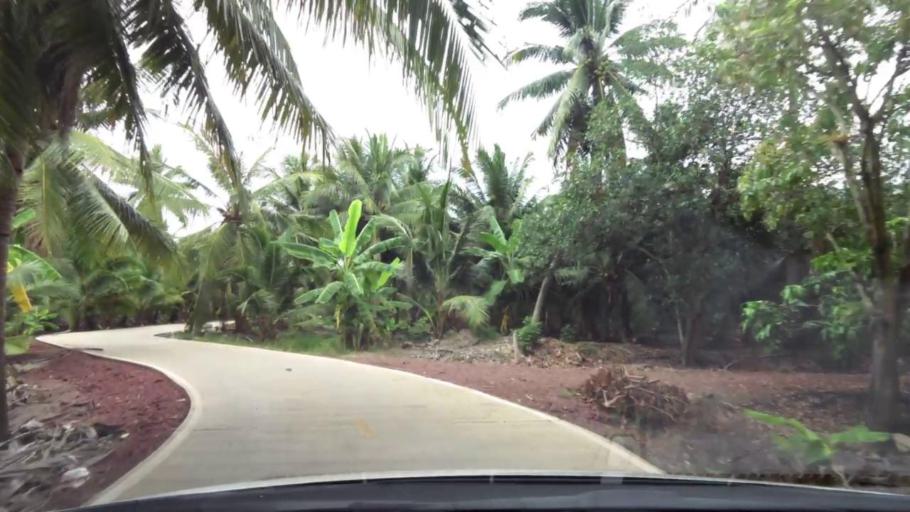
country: TH
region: Ratchaburi
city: Damnoen Saduak
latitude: 13.5489
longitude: 99.9900
